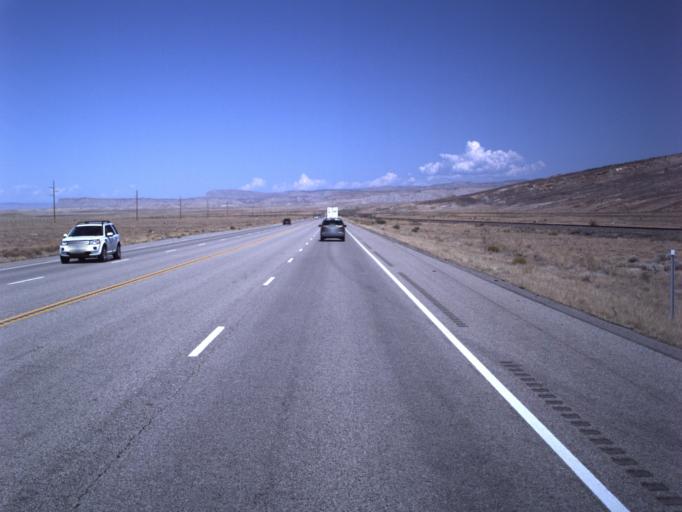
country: US
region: Utah
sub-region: Grand County
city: Moab
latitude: 38.8269
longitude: -109.7831
